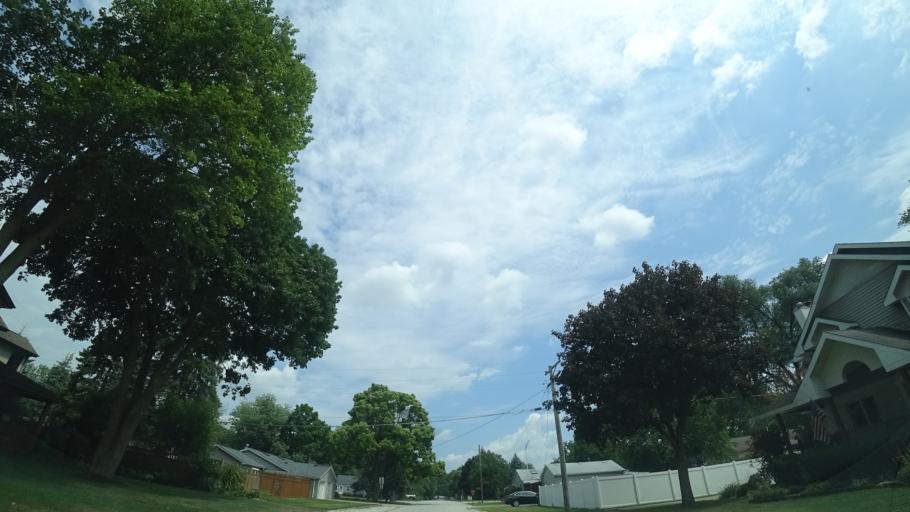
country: US
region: Illinois
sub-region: Cook County
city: Worth
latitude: 41.6865
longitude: -87.7894
